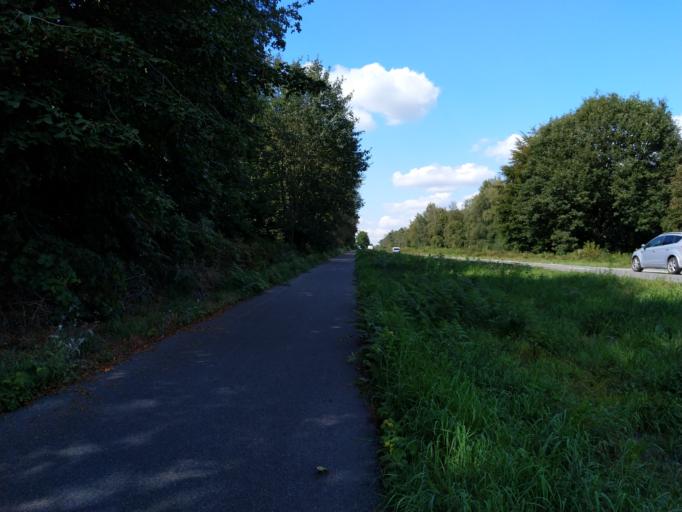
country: BE
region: Wallonia
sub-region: Province du Hainaut
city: Saint-Ghislain
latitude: 50.4857
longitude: 3.8100
